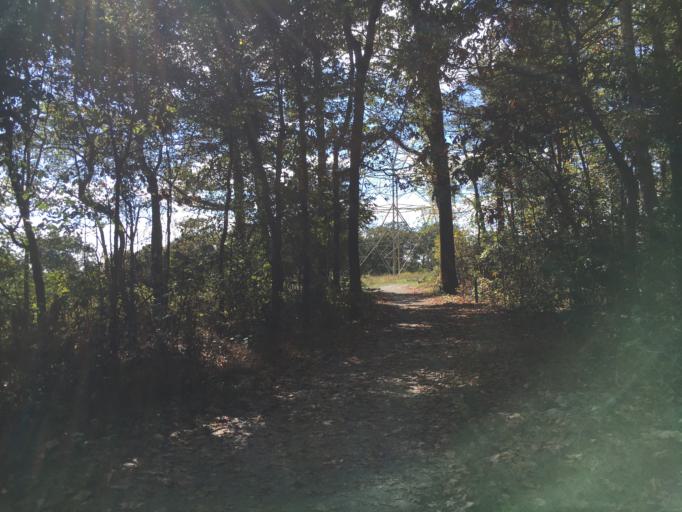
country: US
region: Pennsylvania
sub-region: York County
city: Yorklyn
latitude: 40.0106
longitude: -76.6434
